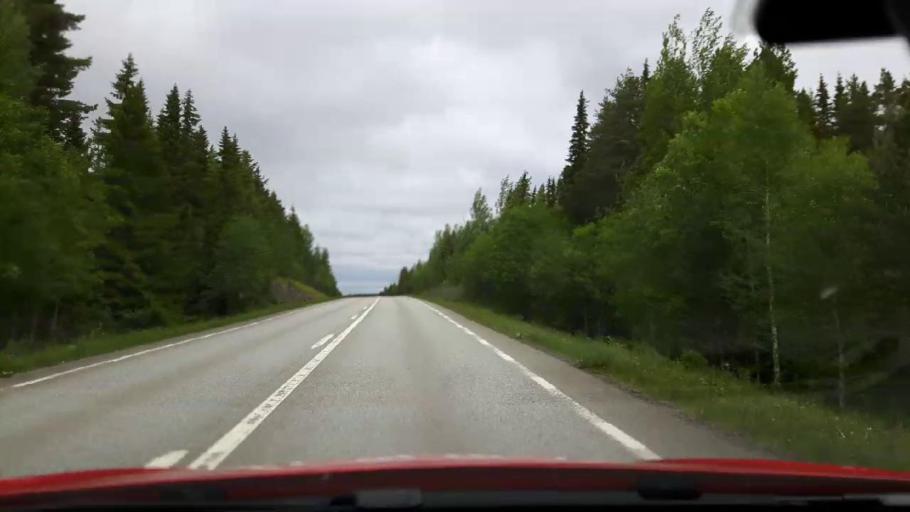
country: SE
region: Jaemtland
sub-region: Krokoms Kommun
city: Krokom
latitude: 63.5004
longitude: 14.5130
